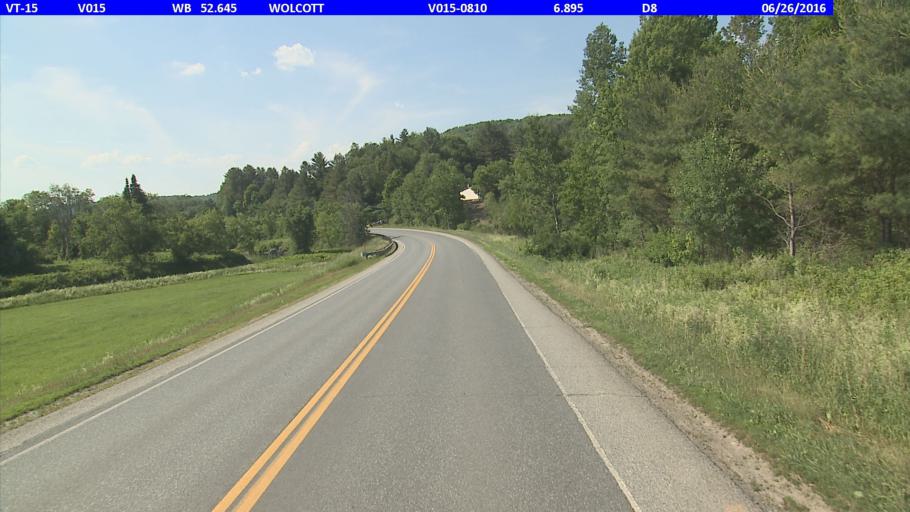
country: US
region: Vermont
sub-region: Caledonia County
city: Hardwick
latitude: 44.5267
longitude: -72.4202
